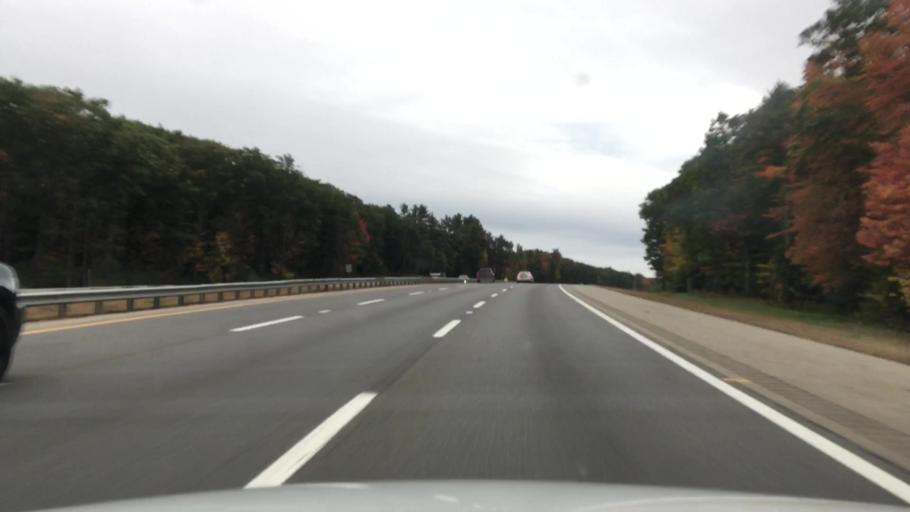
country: US
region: Maine
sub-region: York County
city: Ogunquit
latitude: 43.2587
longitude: -70.6201
